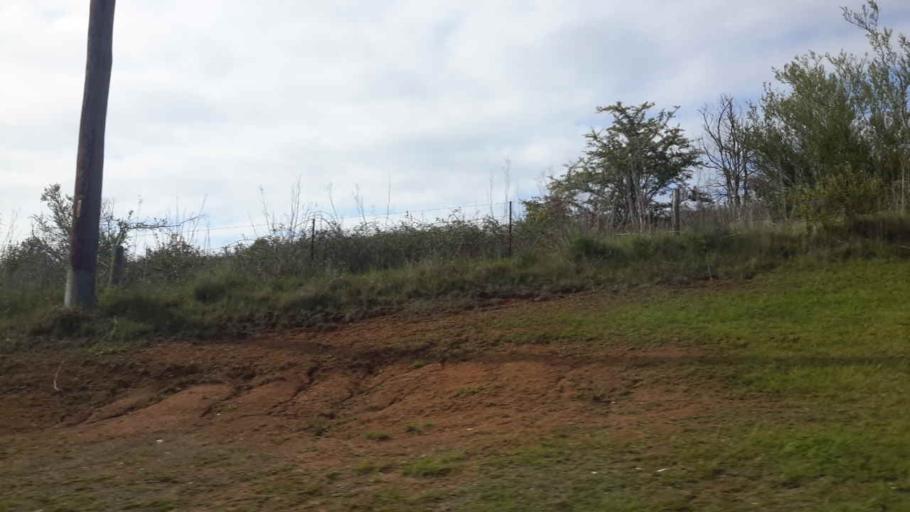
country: AU
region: New South Wales
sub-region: Campbelltown Municipality
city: Glen Alpine
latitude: -34.1086
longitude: 150.7567
